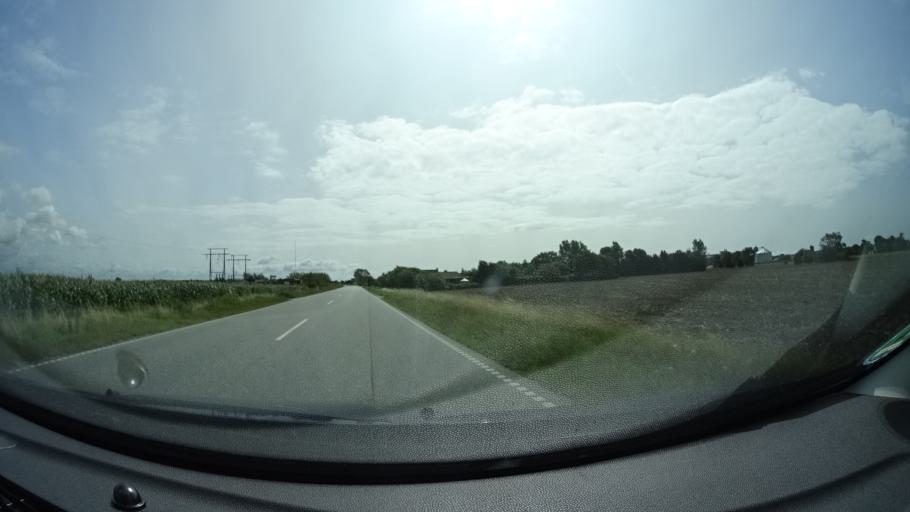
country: DE
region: Schleswig-Holstein
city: Rodenas
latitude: 54.9682
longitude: 8.7014
